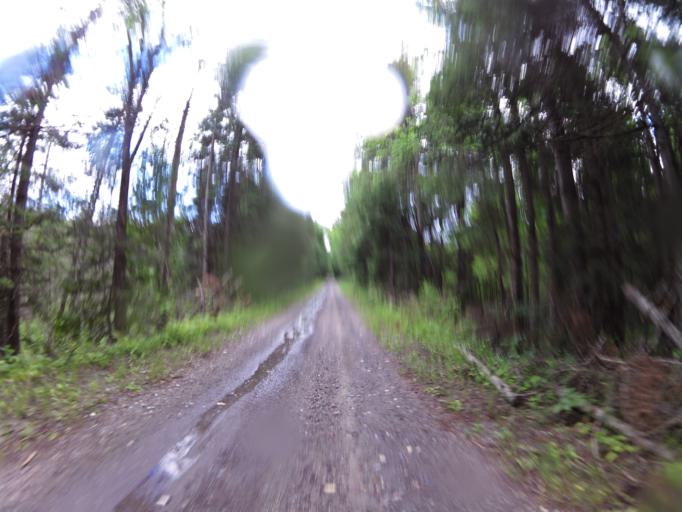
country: CA
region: Ontario
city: Renfrew
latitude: 45.0847
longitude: -76.7209
